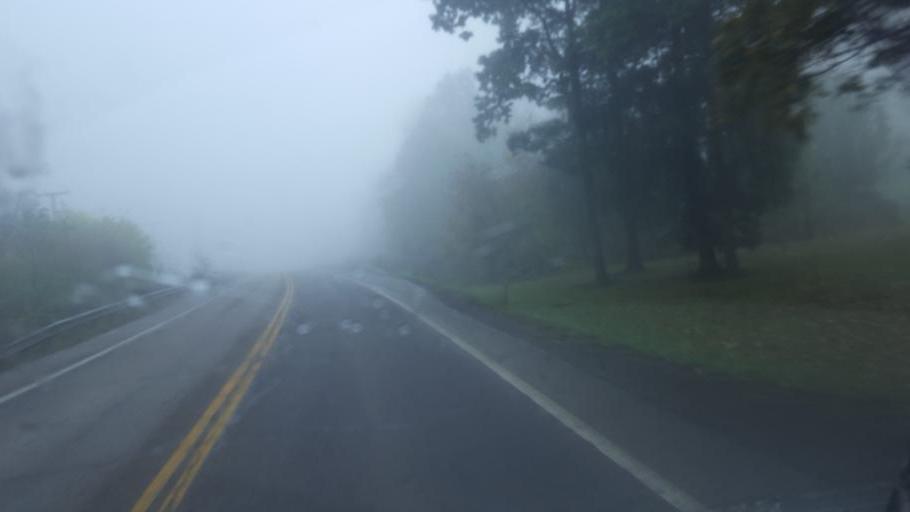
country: US
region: Ohio
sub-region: Tuscarawas County
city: Dover
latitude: 40.5189
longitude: -81.5055
